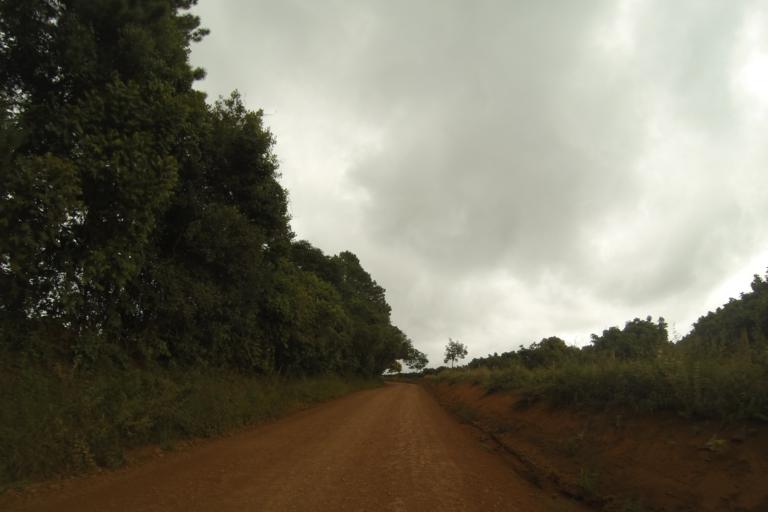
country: BR
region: Minas Gerais
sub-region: Campos Altos
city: Campos Altos
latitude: -19.8012
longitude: -46.3541
